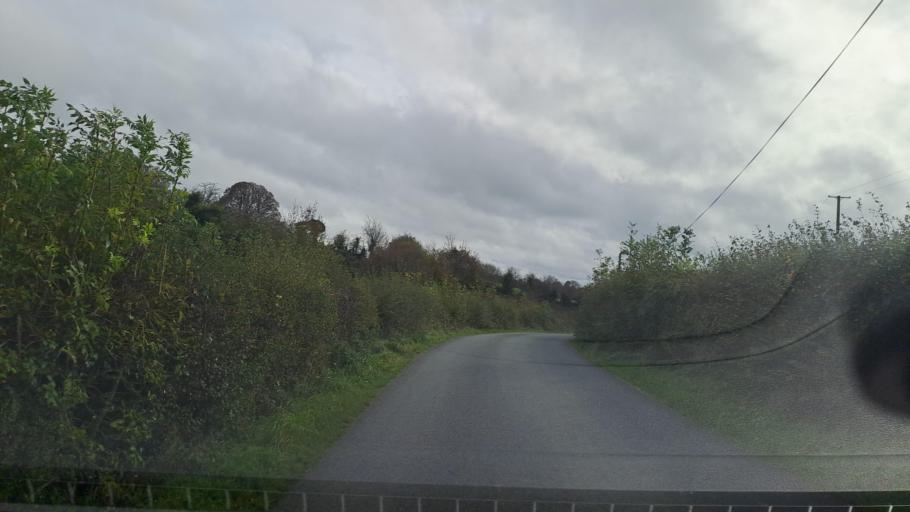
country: IE
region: Ulster
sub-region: An Cabhan
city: Bailieborough
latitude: 54.0158
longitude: -6.8993
